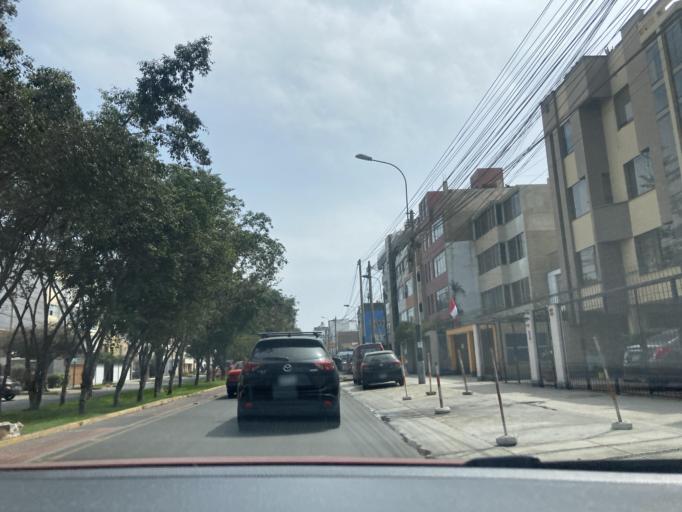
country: PE
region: Lima
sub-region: Lima
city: Surco
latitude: -12.1317
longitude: -76.9868
